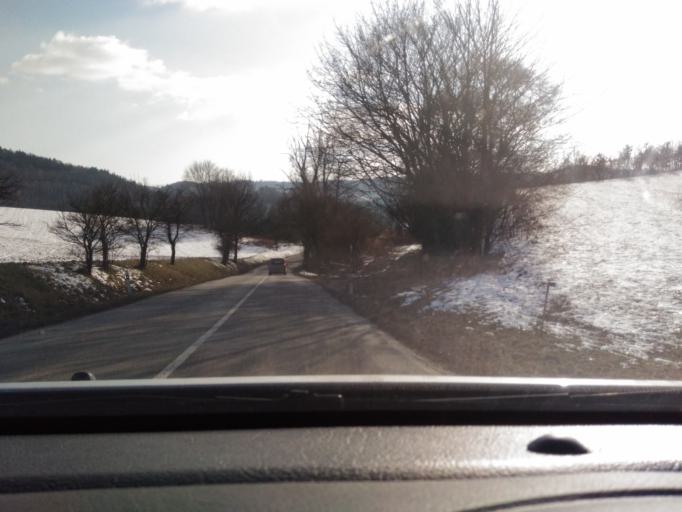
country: CZ
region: South Moravian
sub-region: Okres Brno-Venkov
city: Nedvedice
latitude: 49.4121
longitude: 16.3514
